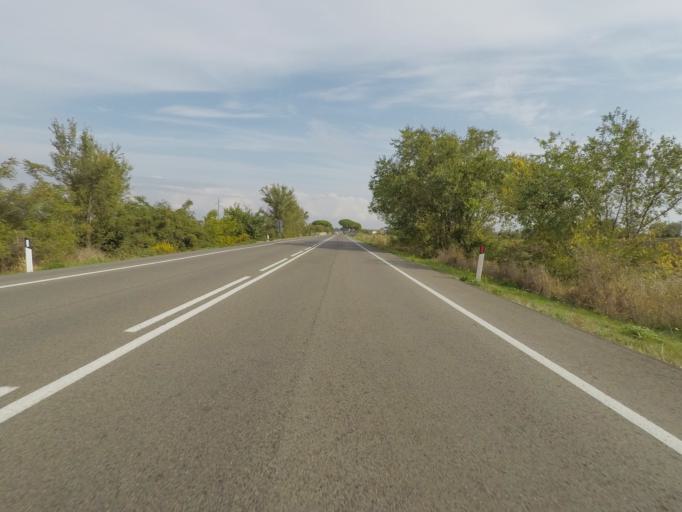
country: IT
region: Tuscany
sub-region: Provincia di Grosseto
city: Capalbio
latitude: 42.4148
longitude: 11.3976
